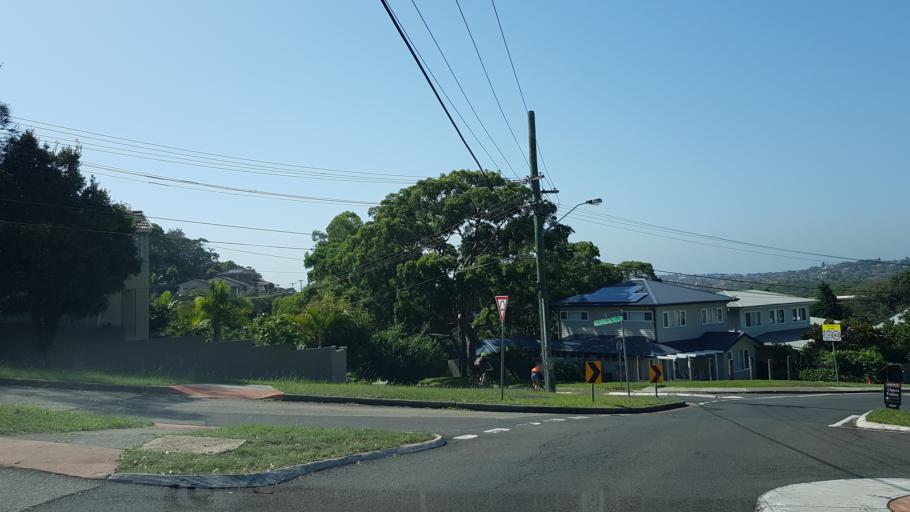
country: AU
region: New South Wales
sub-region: Warringah
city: Dee Why
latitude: -33.7386
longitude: 151.2914
